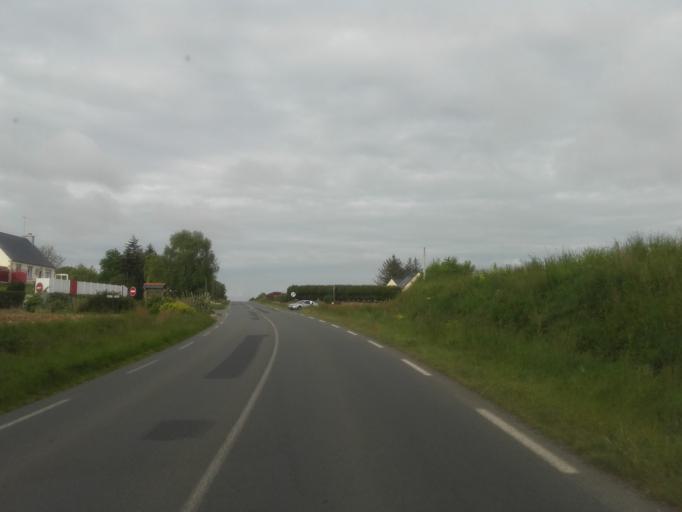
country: FR
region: Brittany
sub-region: Departement des Cotes-d'Armor
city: Saint-Agathon
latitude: 48.5784
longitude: -3.0718
